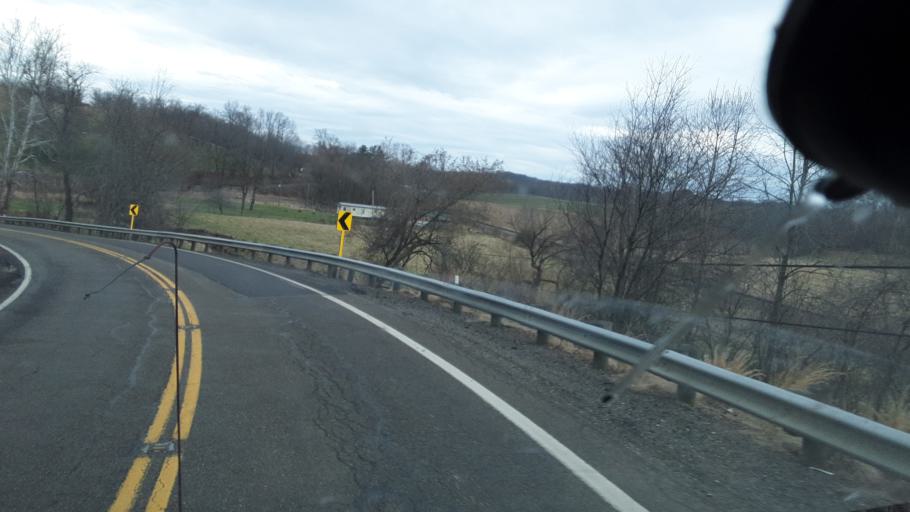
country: US
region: Ohio
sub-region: Coshocton County
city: West Lafayette
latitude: 40.3407
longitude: -81.7354
